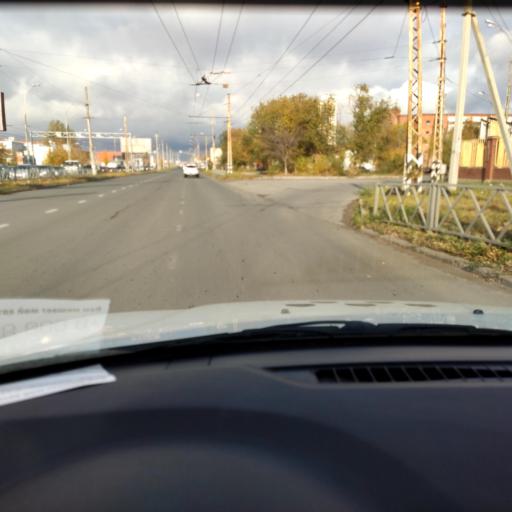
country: RU
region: Samara
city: Tol'yatti
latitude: 53.5365
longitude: 49.2994
